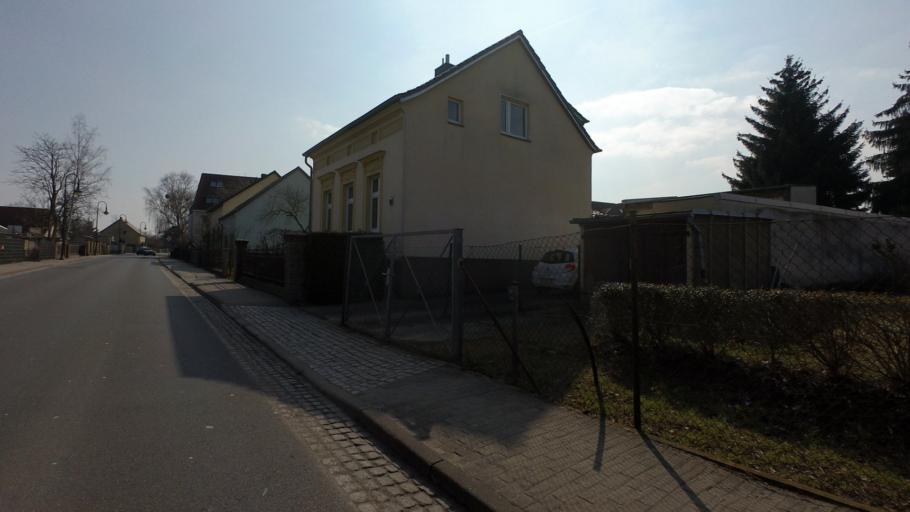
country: DE
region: Brandenburg
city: Werder
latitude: 52.3678
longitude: 12.9384
